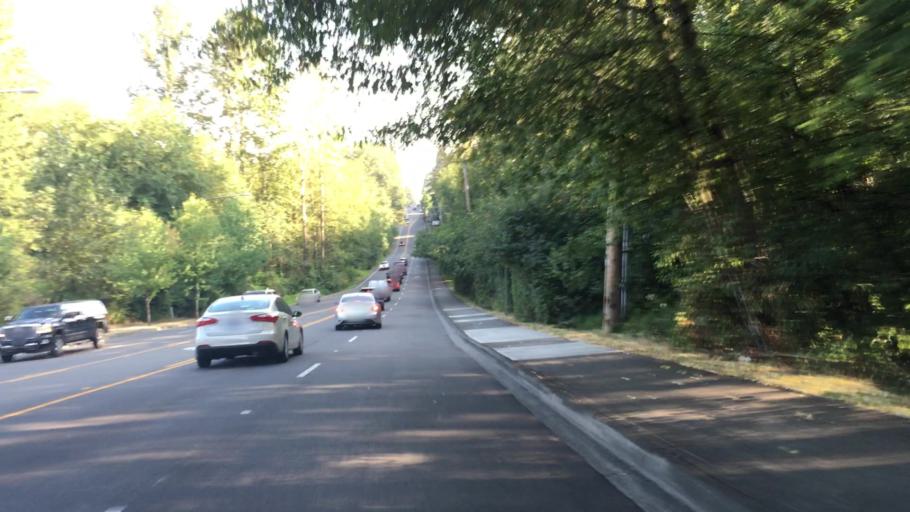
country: US
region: Washington
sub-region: Pierce County
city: Fife Heights
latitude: 47.2888
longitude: -122.3347
